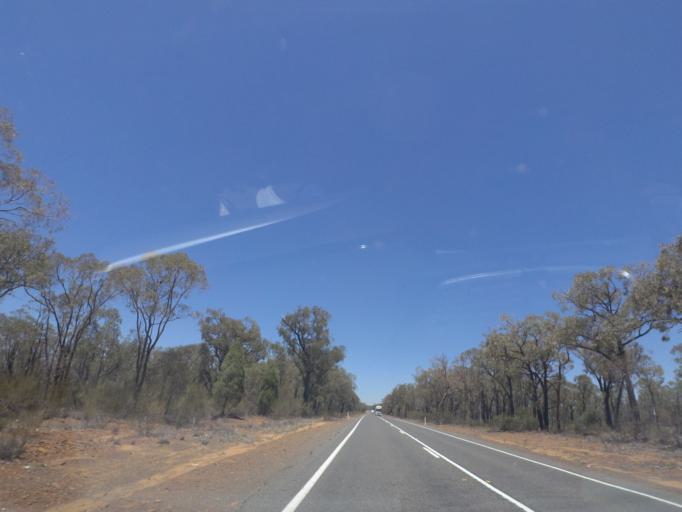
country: AU
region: New South Wales
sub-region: Narrabri
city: Narrabri
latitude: -30.7039
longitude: 149.5332
